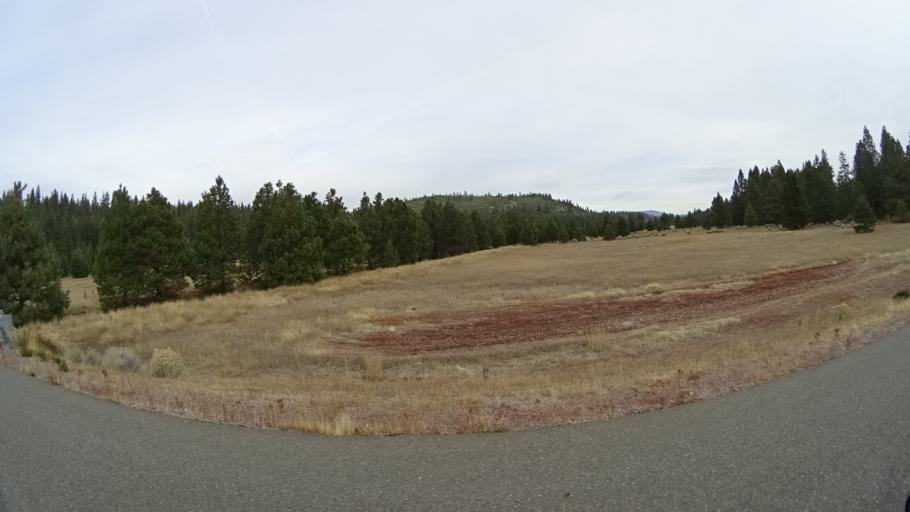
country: US
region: California
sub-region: Siskiyou County
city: Weed
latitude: 41.3945
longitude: -122.3887
